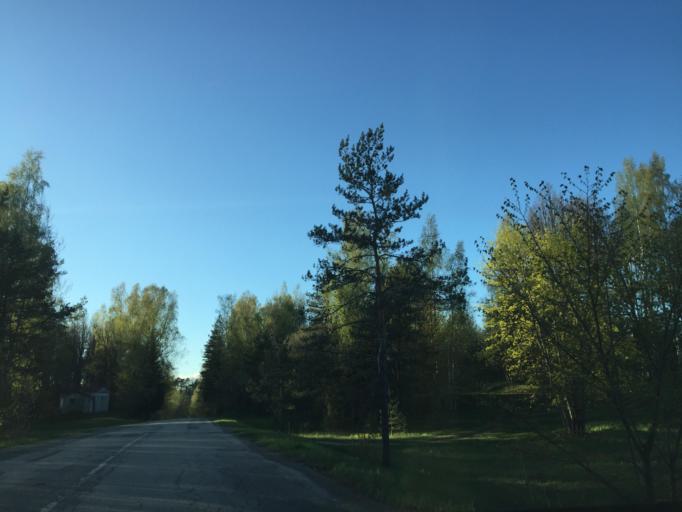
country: LV
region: Vecpiebalga
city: Vecpiebalga
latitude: 56.8605
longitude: 25.8475
